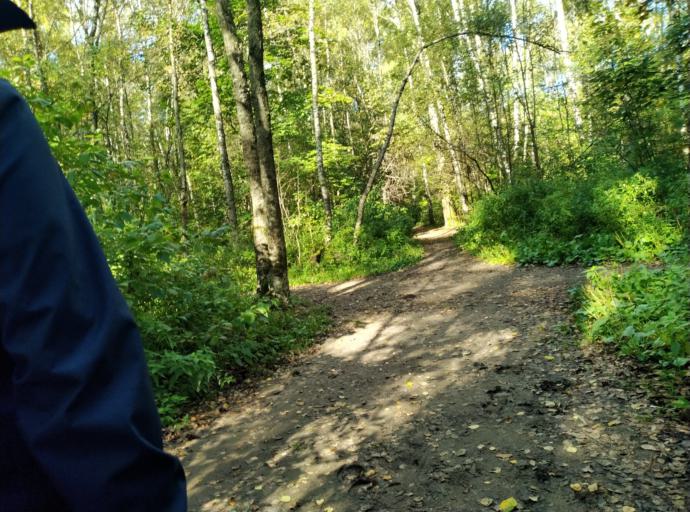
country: RU
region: Moscow
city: Khimki
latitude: 55.8675
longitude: 37.4287
